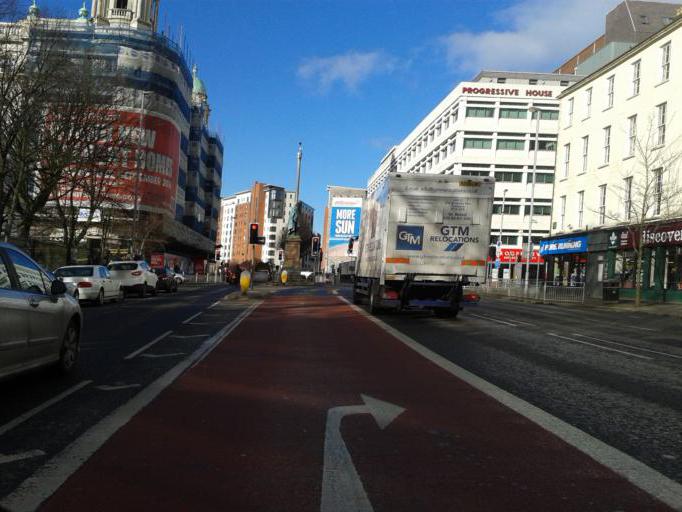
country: GB
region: Northern Ireland
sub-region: City of Belfast
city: Belfast
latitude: 54.5965
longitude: -5.9348
